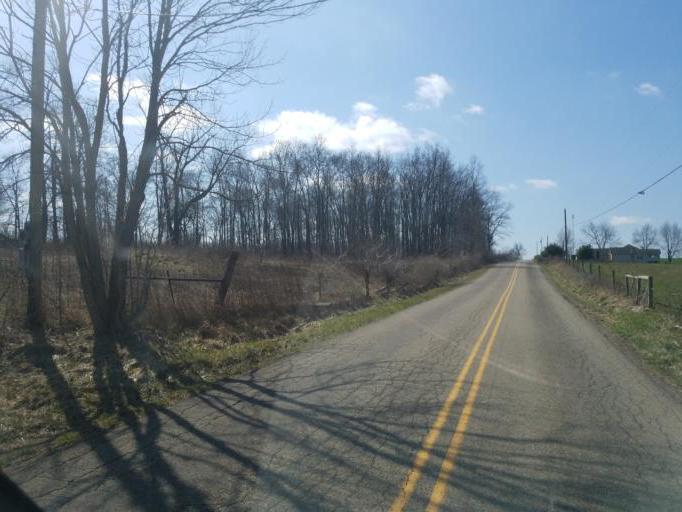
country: US
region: Ohio
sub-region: Knox County
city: Gambier
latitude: 40.2728
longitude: -82.3218
